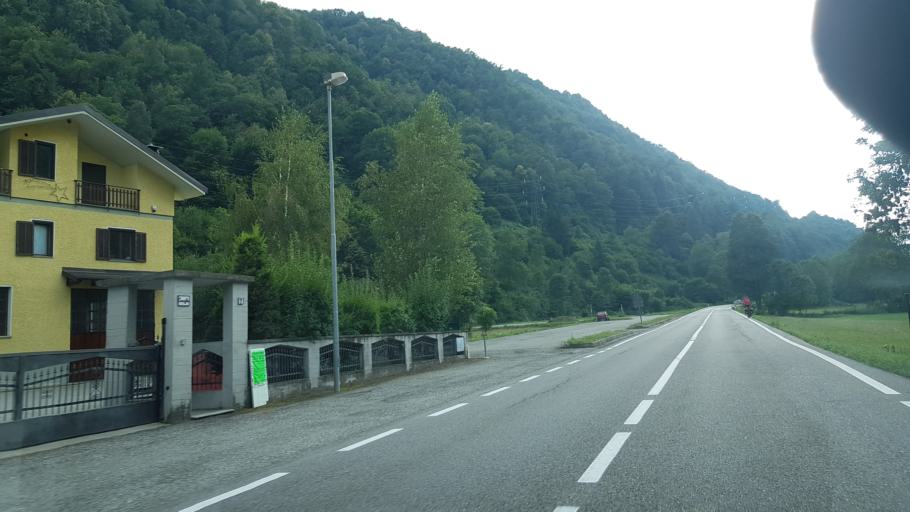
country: IT
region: Piedmont
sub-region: Provincia di Cuneo
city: Frassino
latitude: 44.5690
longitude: 7.2917
